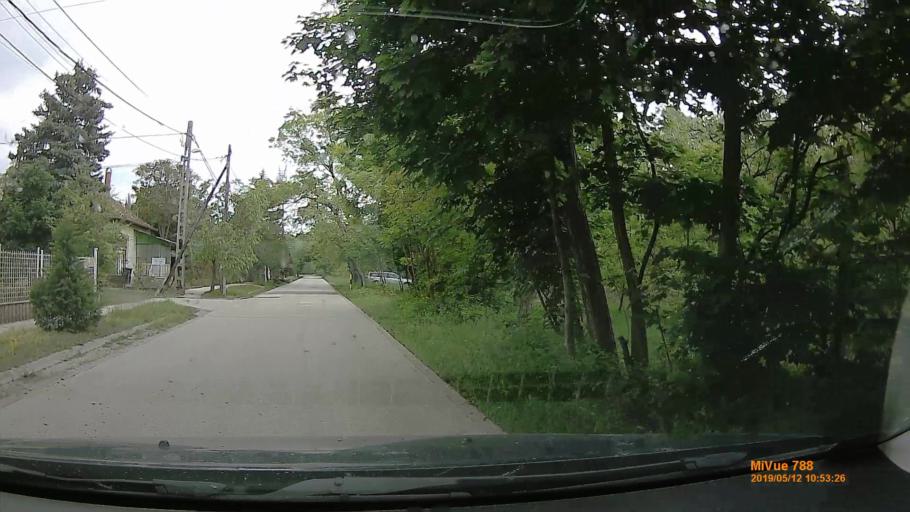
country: HU
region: Budapest
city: Budapest XVII. keruelet
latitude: 47.4768
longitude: 19.2212
